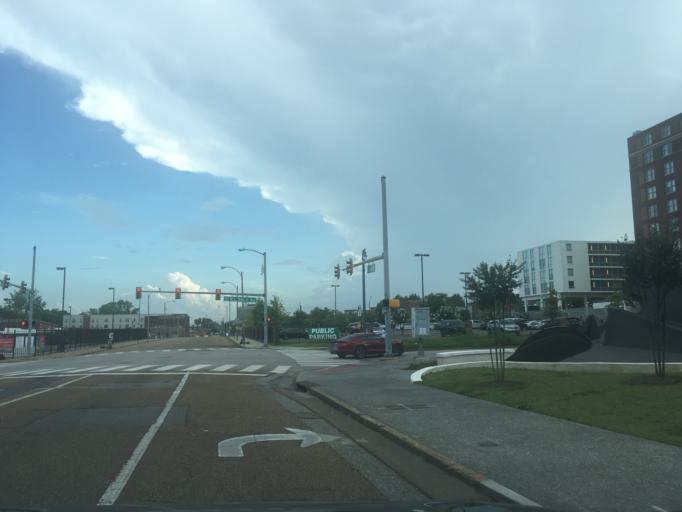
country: US
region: Tennessee
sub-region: Shelby County
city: Memphis
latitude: 35.1386
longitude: -90.0542
